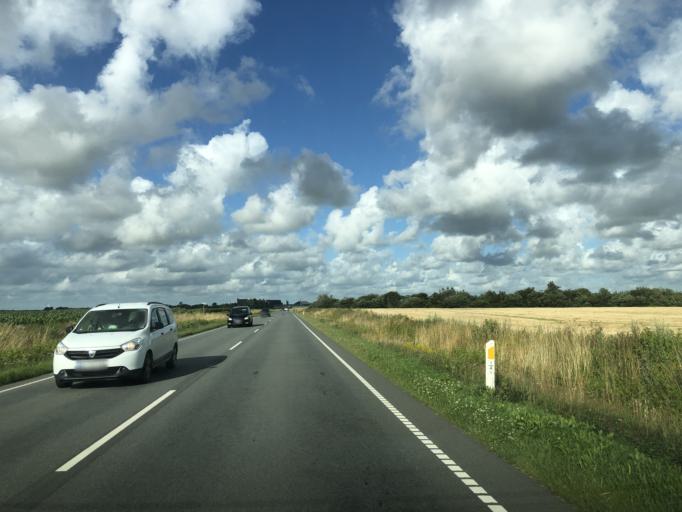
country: DK
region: Central Jutland
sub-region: Lemvig Kommune
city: Lemvig
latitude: 56.5069
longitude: 8.2861
